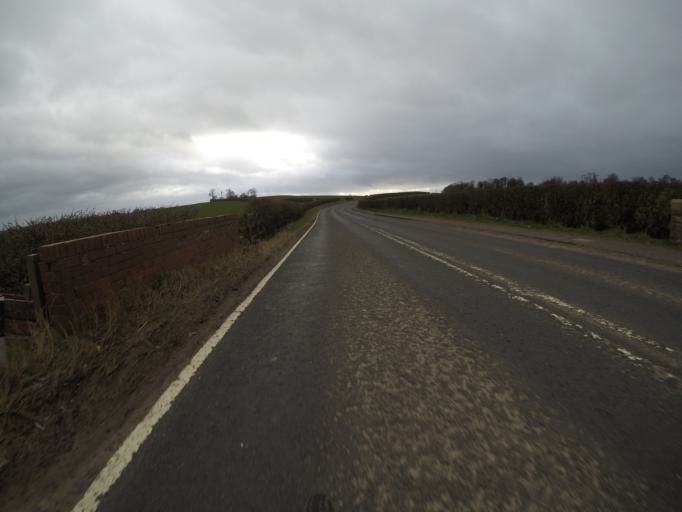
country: GB
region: Scotland
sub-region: East Ayrshire
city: Crosshouse
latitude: 55.6116
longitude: -4.5650
